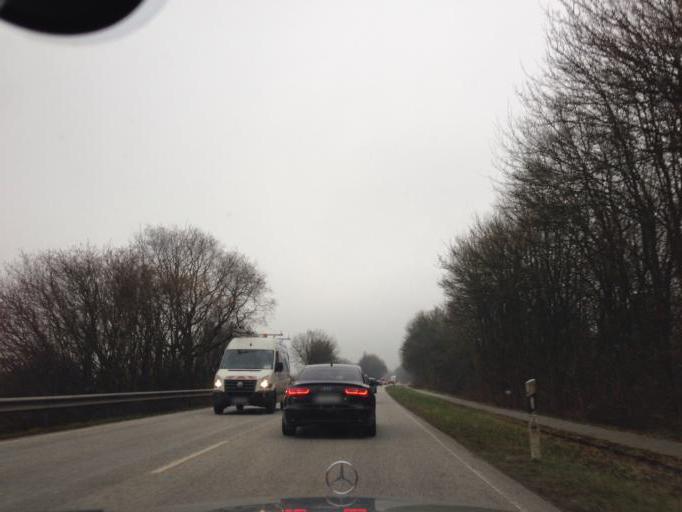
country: DE
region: Schleswig-Holstein
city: Kirchbarkau
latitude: 54.2036
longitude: 10.1518
